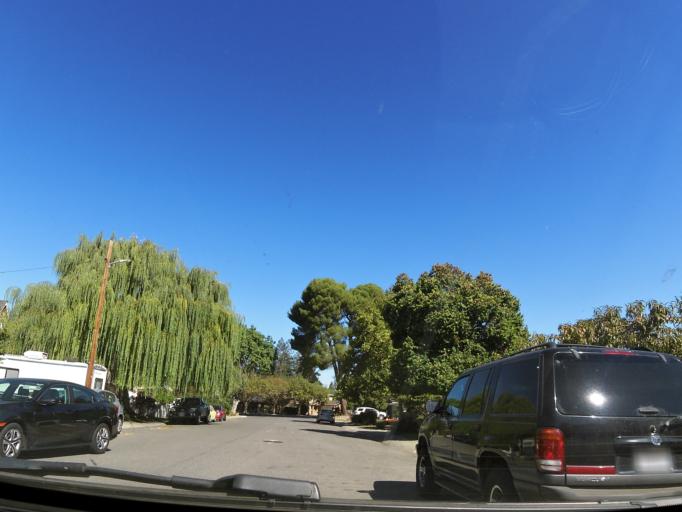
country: US
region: California
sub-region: Santa Clara County
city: Buena Vista
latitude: 37.2996
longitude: -121.9188
